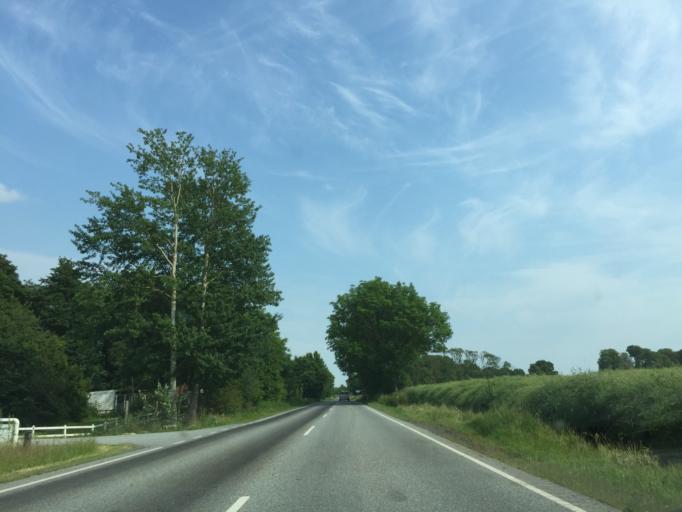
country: DK
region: Central Jutland
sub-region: Syddjurs Kommune
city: Ronde
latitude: 56.3124
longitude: 10.4358
